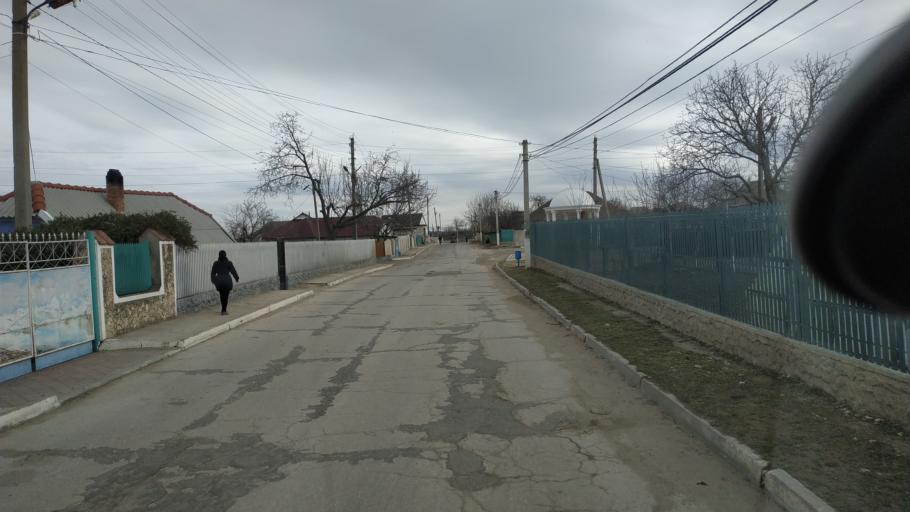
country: MD
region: Telenesti
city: Cocieri
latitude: 47.3829
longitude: 29.1166
